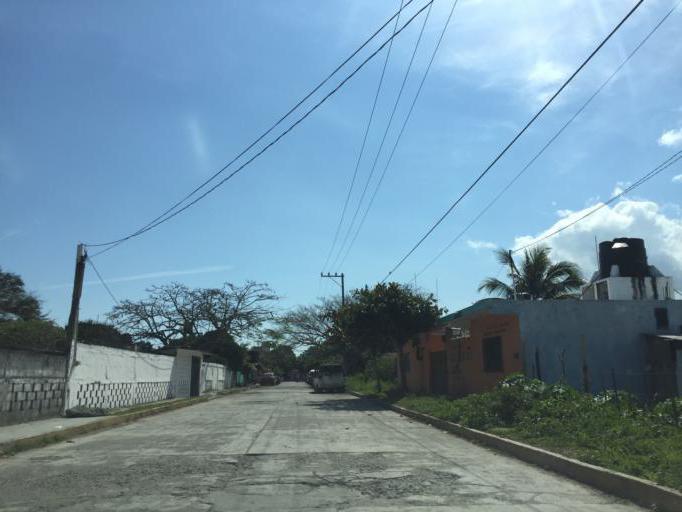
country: MX
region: Veracruz
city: Tecolutla
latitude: 20.4807
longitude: -97.0108
